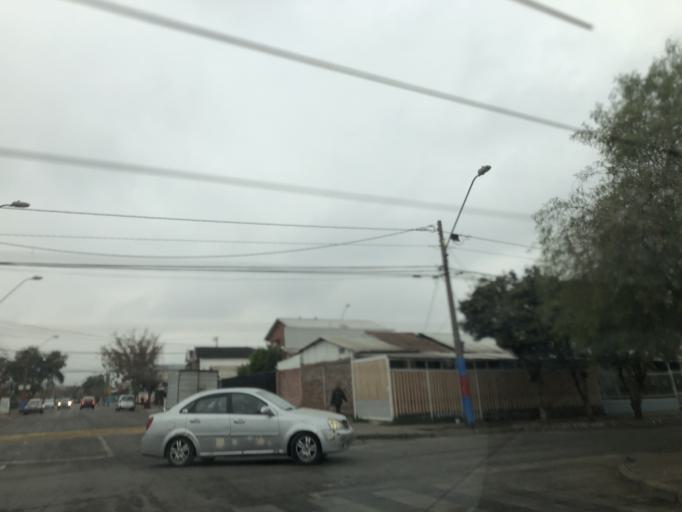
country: CL
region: Santiago Metropolitan
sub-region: Provincia de Cordillera
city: Puente Alto
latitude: -33.5830
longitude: -70.5926
